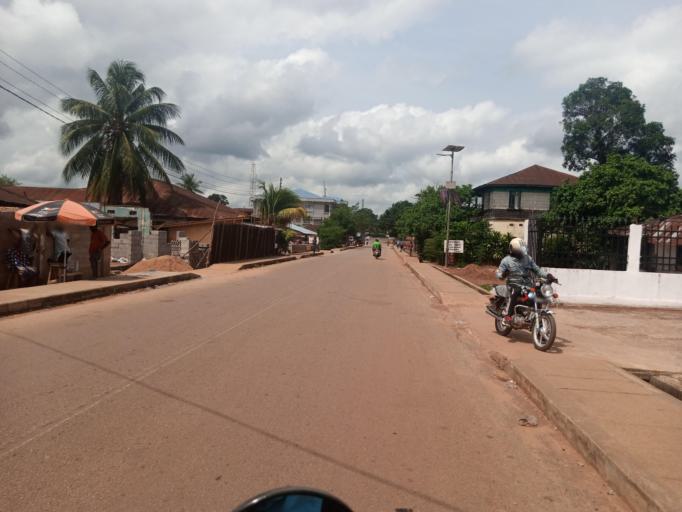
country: SL
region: Southern Province
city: Bo
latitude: 7.9690
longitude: -11.7405
